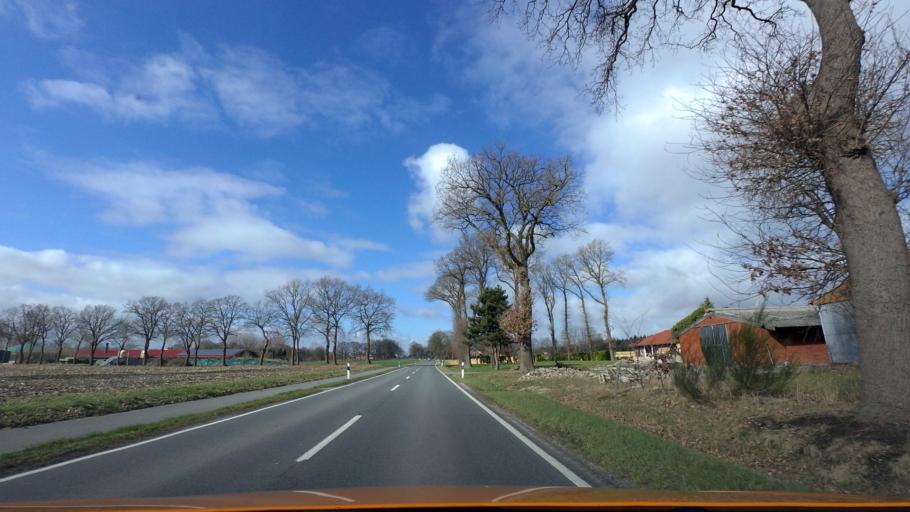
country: DE
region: Lower Saxony
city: Bosel
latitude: 53.0079
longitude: 7.9358
